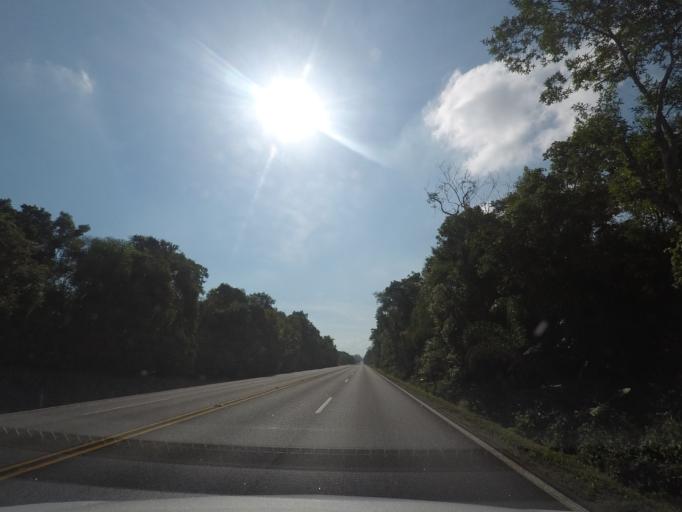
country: BR
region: Parana
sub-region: Pontal Do Parana
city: Pontal do Parana
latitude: -25.6225
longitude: -48.5990
